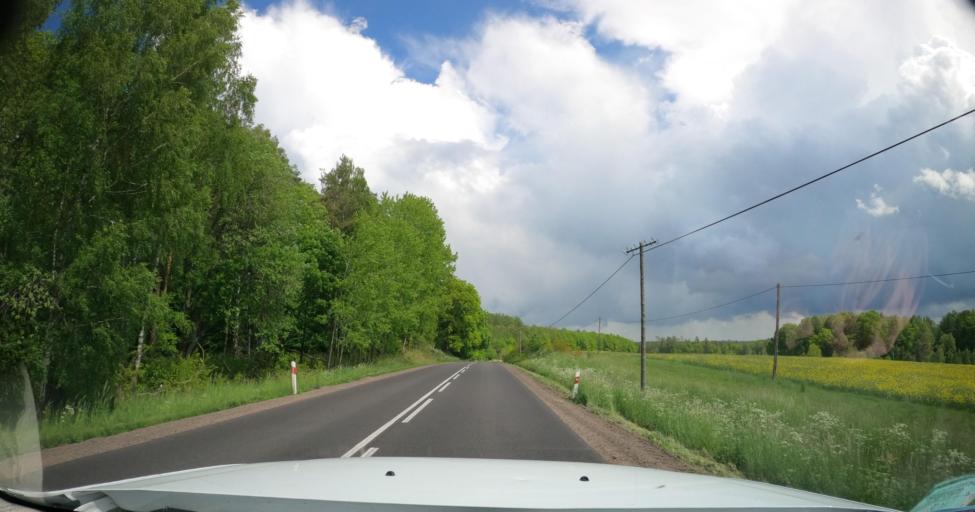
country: PL
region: Pomeranian Voivodeship
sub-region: Powiat bytowski
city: Czarna Dabrowka
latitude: 54.3456
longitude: 17.5884
